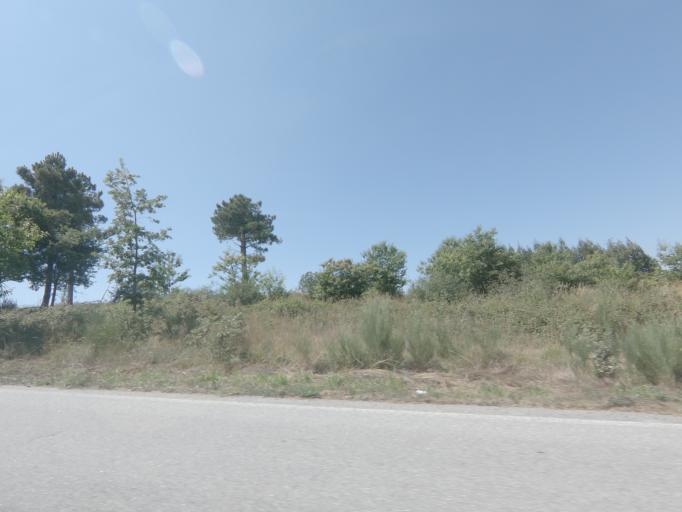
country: PT
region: Viseu
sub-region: Tarouca
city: Tarouca
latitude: 40.9915
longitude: -7.8397
